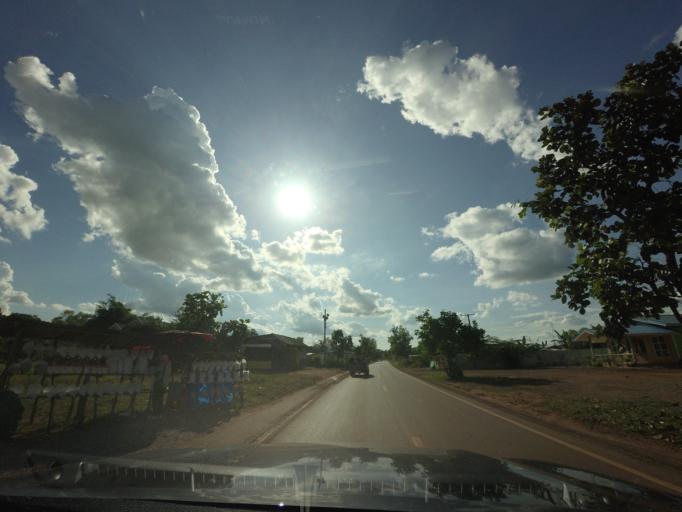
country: TH
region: Changwat Udon Thani
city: Ban Dung
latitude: 17.7448
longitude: 103.3208
